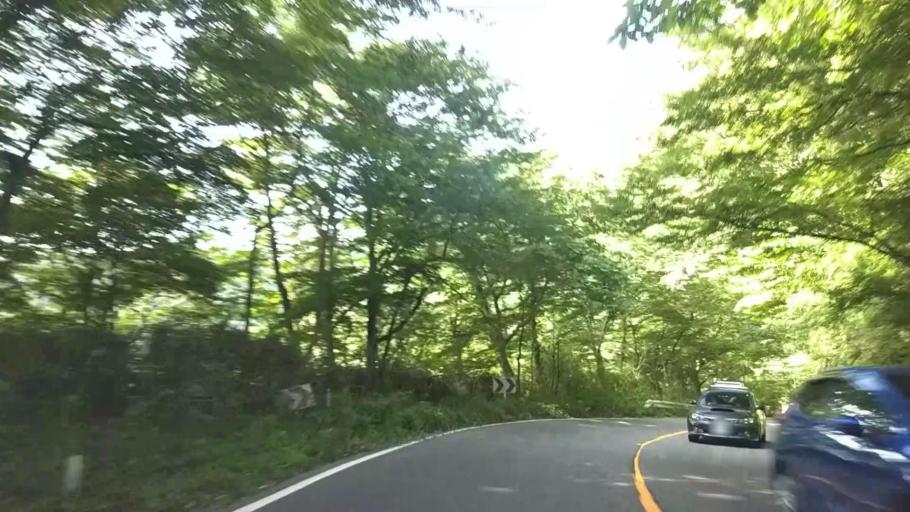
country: JP
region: Kanagawa
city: Hakone
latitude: 35.2253
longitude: 139.0042
